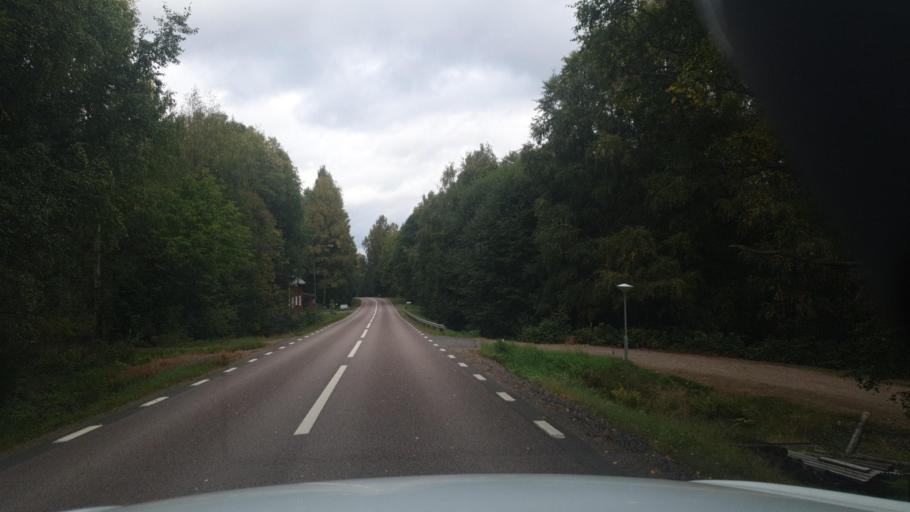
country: SE
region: Vaermland
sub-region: Sunne Kommun
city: Sunne
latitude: 59.8831
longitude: 12.9257
